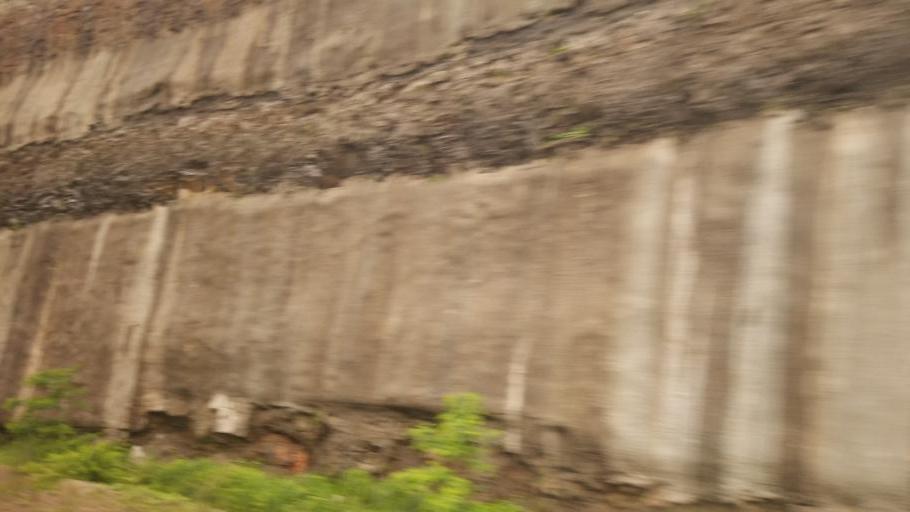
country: US
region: Pennsylvania
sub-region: Somerset County
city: Milford
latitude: 39.8415
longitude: -79.2471
